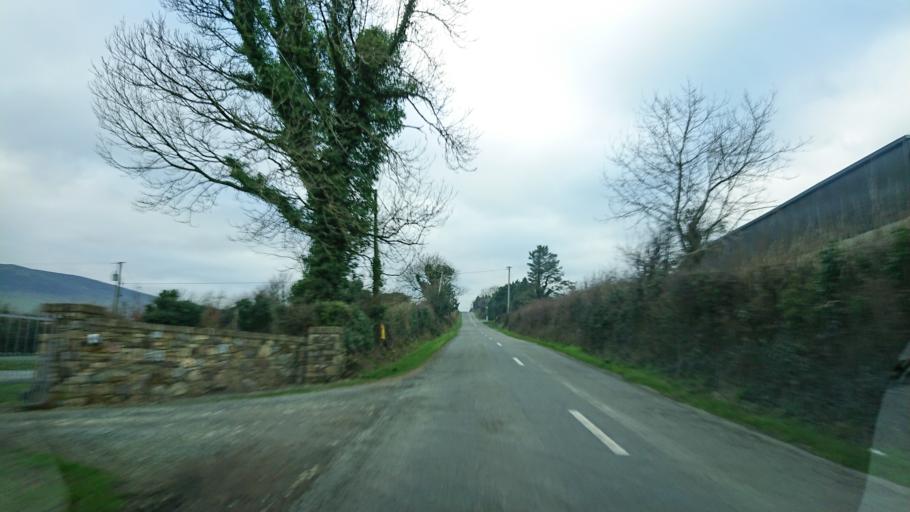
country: IE
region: Munster
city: Carrick-on-Suir
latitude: 52.3194
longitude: -7.5568
